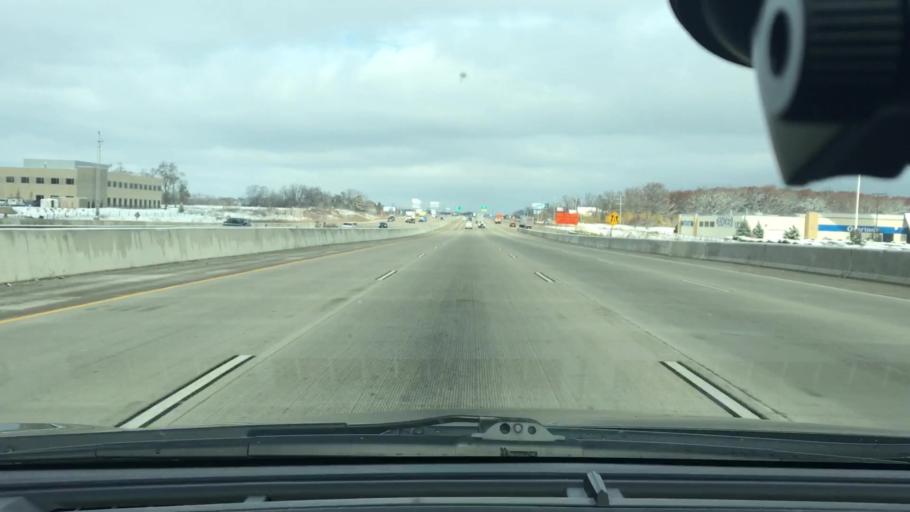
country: US
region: Wisconsin
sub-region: Kenosha County
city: Pleasant Prairie
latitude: 42.5719
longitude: -87.9527
